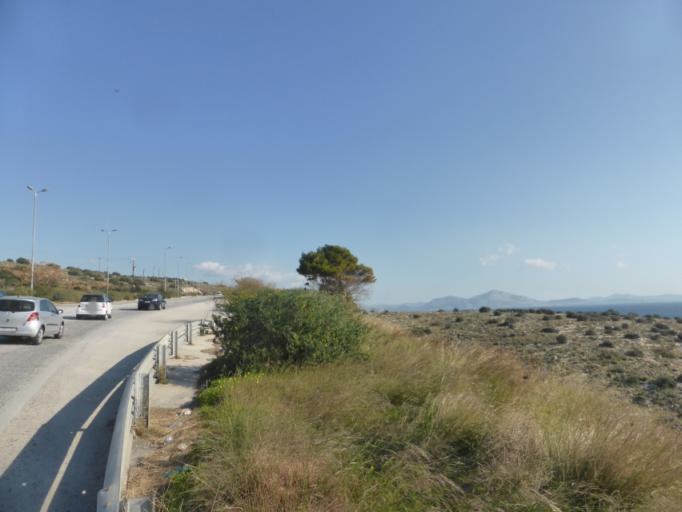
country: GR
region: Attica
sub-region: Nomarchia Anatolikis Attikis
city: Vouliagmeni
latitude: 37.8018
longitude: 23.7886
